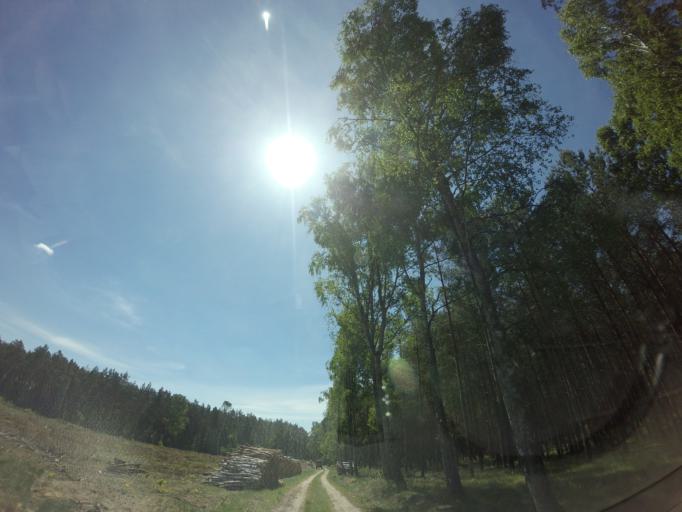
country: PL
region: West Pomeranian Voivodeship
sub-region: Powiat choszczenski
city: Drawno
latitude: 53.2594
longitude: 15.7465
